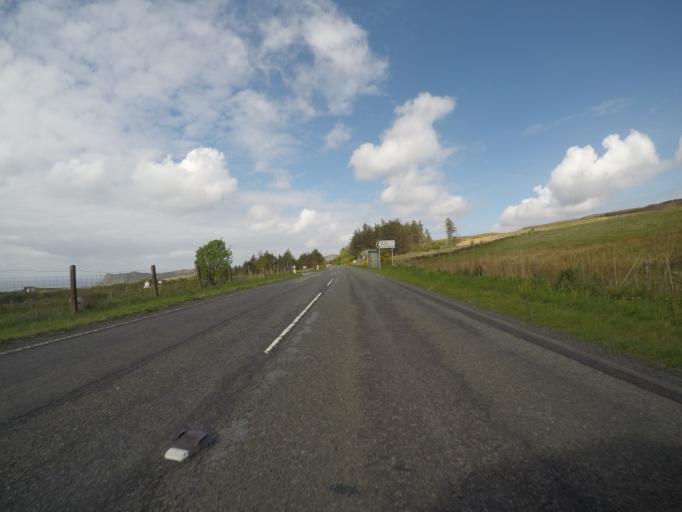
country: GB
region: Scotland
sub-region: Highland
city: Portree
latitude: 57.5670
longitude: -6.3647
